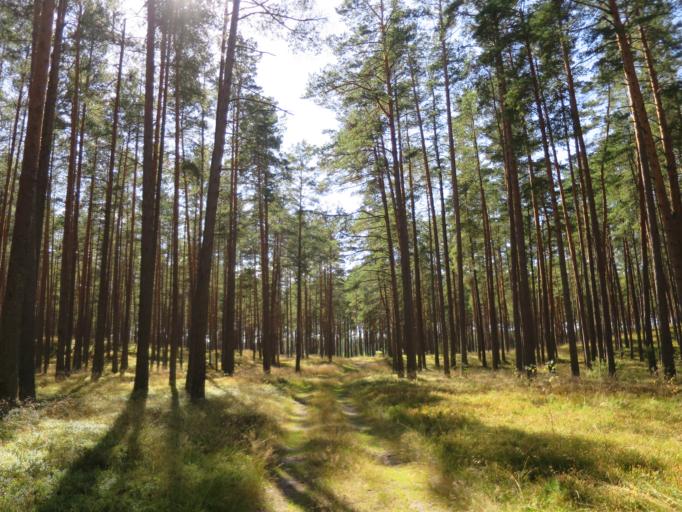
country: LV
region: Riga
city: Jaunciems
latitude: 57.0625
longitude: 24.2282
